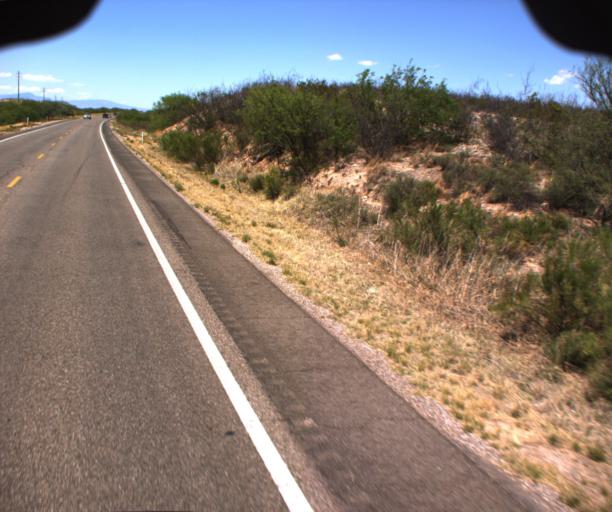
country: US
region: Arizona
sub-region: Cochise County
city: Tombstone
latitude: 31.7897
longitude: -110.1497
